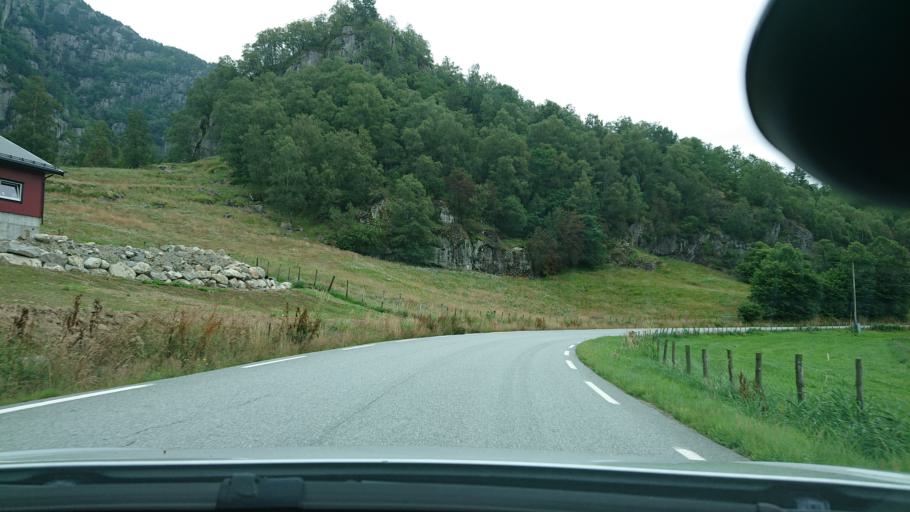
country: NO
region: Rogaland
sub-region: Hjelmeland
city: Hjelmelandsvagen
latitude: 59.2316
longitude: 6.2037
